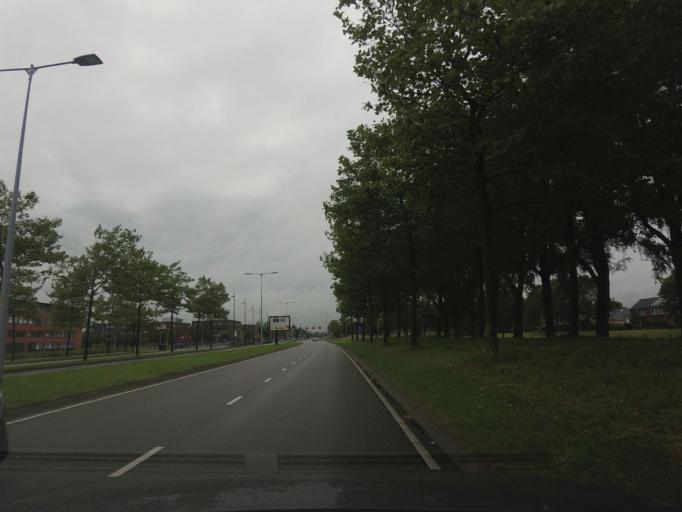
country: NL
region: North Holland
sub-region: Gemeente Haarlemmermeer
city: Hoofddorp
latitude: 52.2946
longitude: 4.6854
